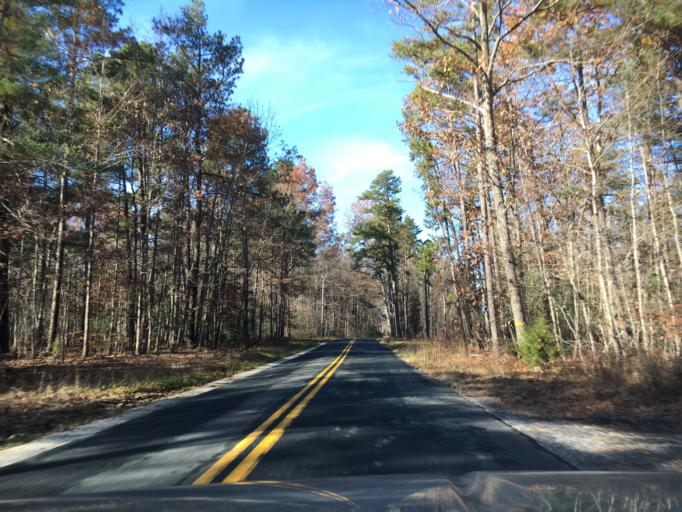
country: US
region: Virginia
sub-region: Buckingham County
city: Buckingham
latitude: 37.4413
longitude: -78.6674
